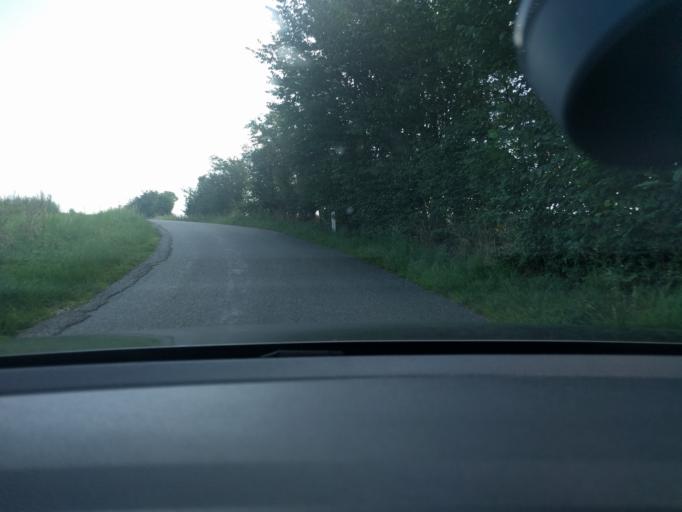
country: DK
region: Central Jutland
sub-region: Viborg Kommune
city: Viborg
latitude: 56.5230
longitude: 9.3534
